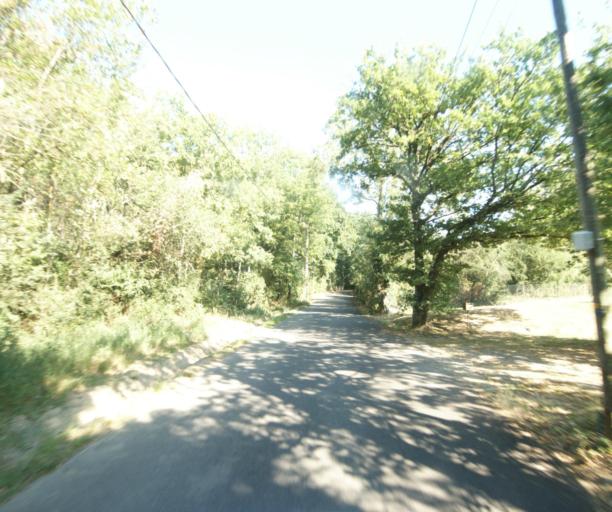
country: FR
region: Rhone-Alpes
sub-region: Departement du Rhone
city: Sainte-Consorce
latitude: 45.8007
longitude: 4.6921
